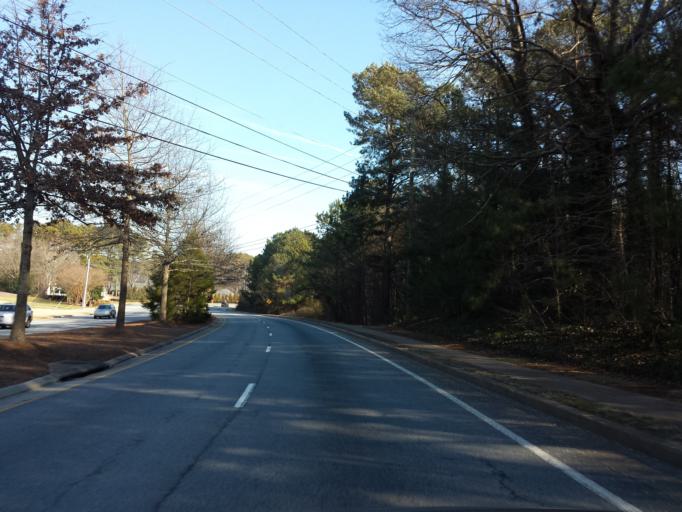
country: US
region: Georgia
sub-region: Cobb County
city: Kennesaw
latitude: 34.0368
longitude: -84.5587
